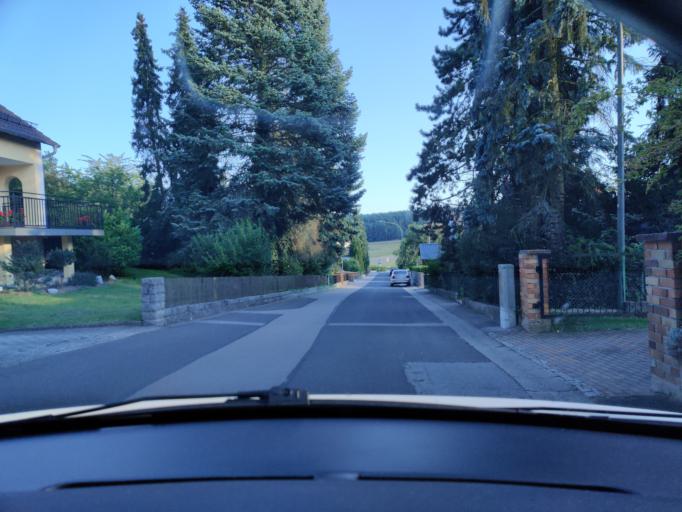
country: DE
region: Bavaria
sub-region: Upper Palatinate
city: Stulln
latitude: 49.4219
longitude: 12.1498
